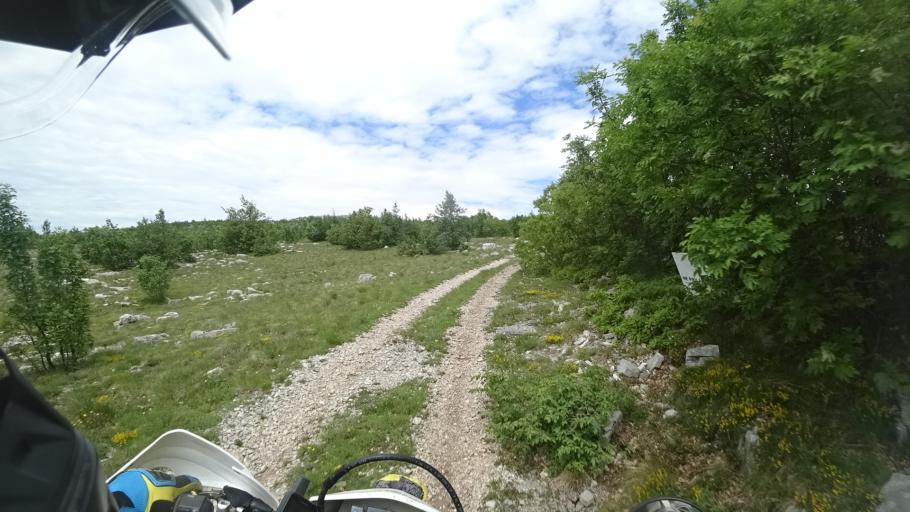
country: HR
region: Splitsko-Dalmatinska
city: Hrvace
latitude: 43.8856
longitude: 16.5890
